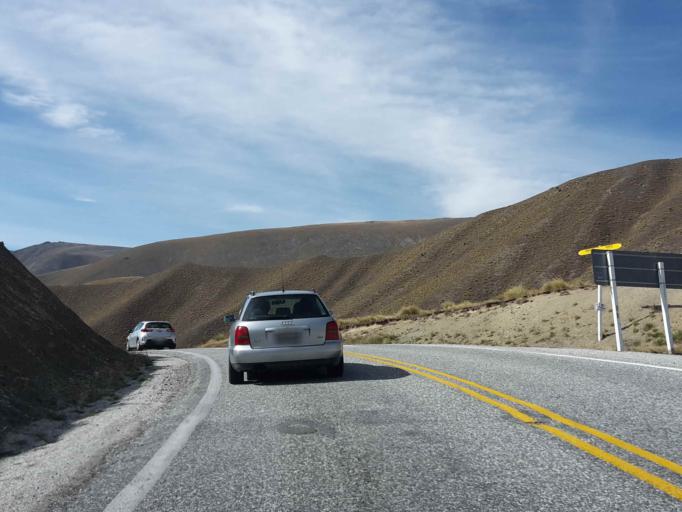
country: NZ
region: Otago
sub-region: Queenstown-Lakes District
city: Wanaka
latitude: -44.5883
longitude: 169.6425
